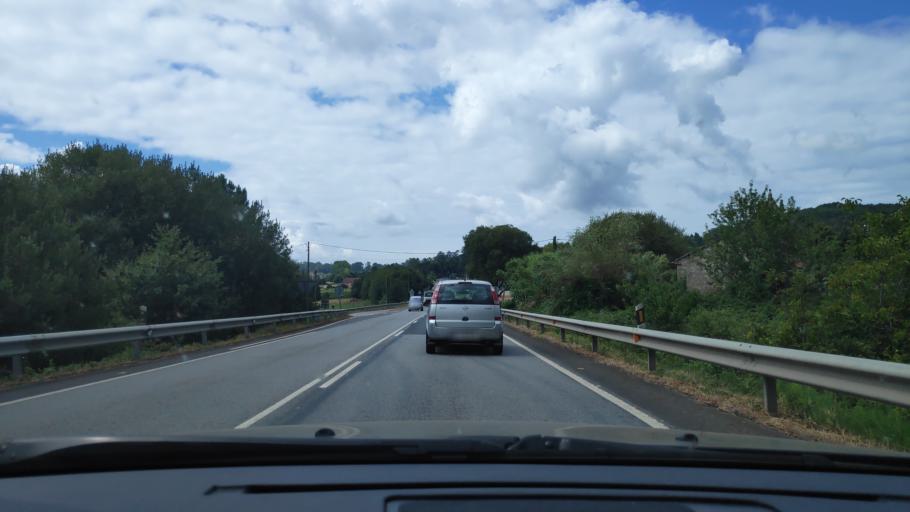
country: ES
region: Galicia
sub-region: Provincia de Pontevedra
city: Portas
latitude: 42.5865
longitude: -8.6929
